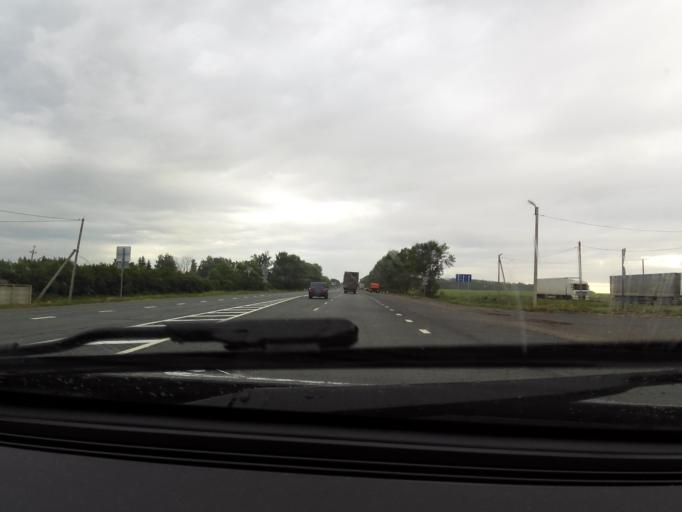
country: RU
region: Chuvashia
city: Yantikovo
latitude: 55.7935
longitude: 47.8093
